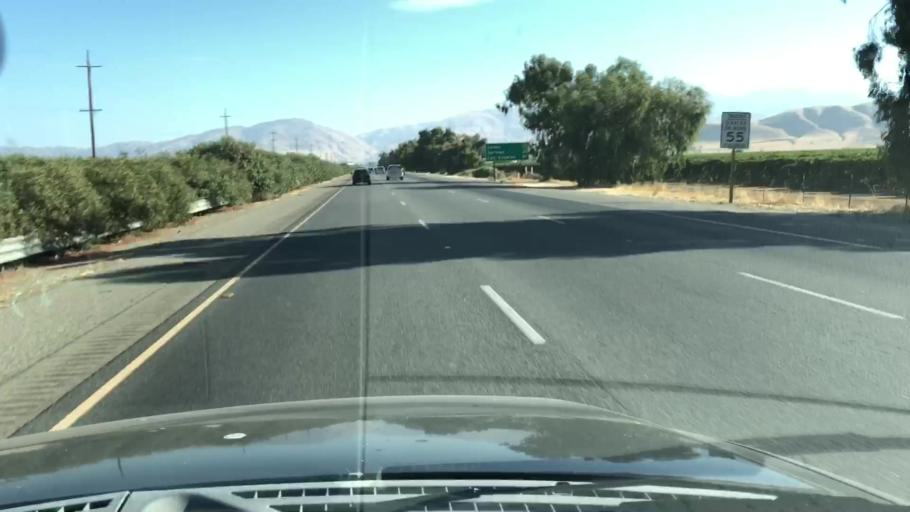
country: US
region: California
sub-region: Kern County
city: Weedpatch
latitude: 35.0477
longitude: -118.9647
